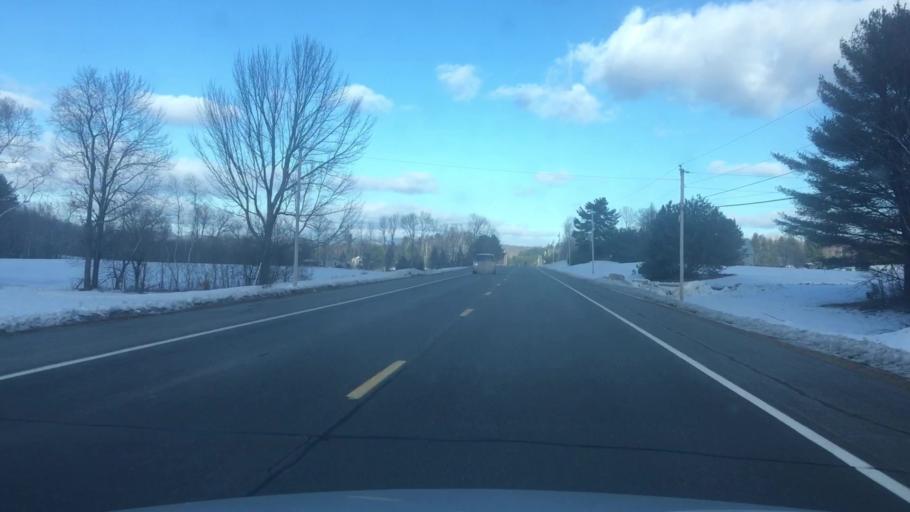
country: US
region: Maine
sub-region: Somerset County
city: Madison
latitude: 45.0170
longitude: -69.8576
